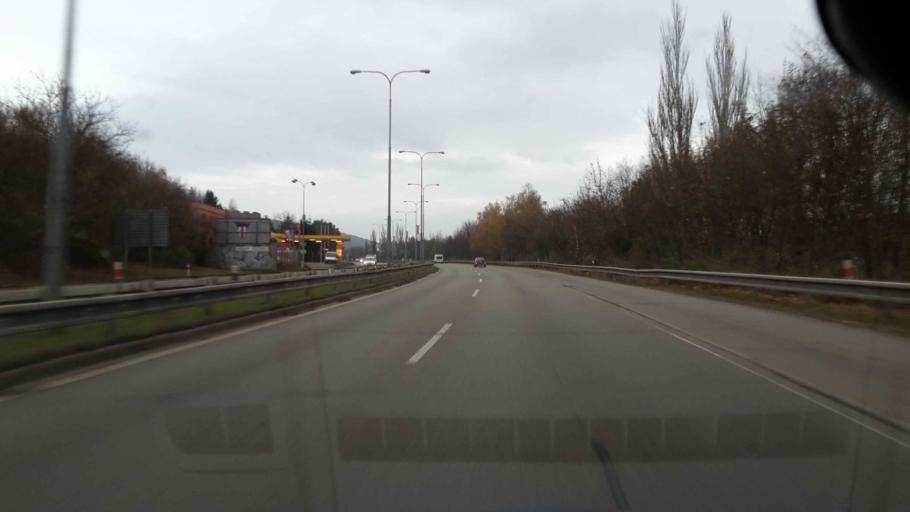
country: CZ
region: South Moravian
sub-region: Mesto Brno
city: Mokra Hora
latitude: 49.2533
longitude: 16.5876
